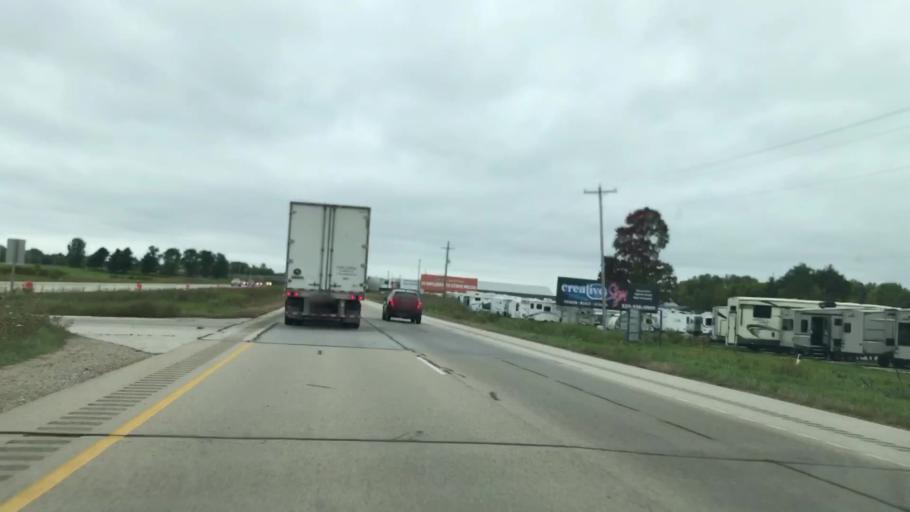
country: US
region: Wisconsin
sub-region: Brown County
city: Suamico
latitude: 44.6682
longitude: -88.0504
